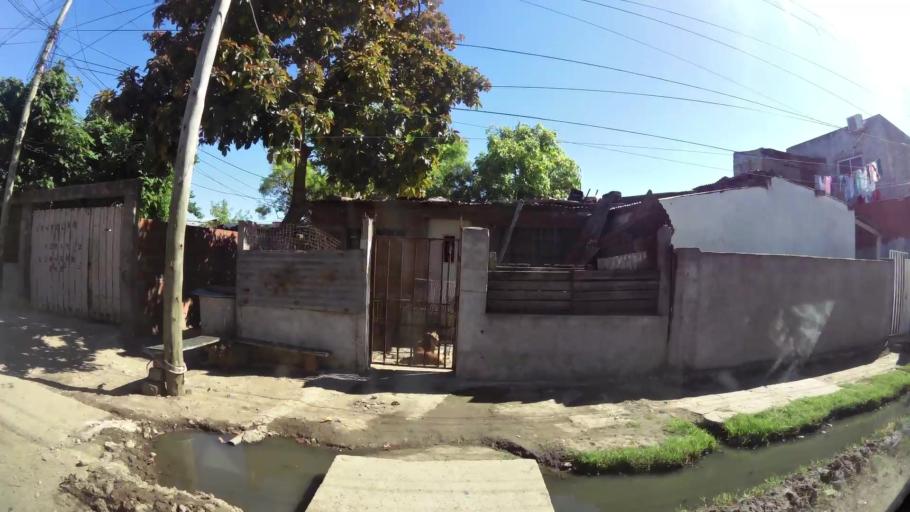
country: AR
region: Santa Fe
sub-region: Departamento de Rosario
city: Rosario
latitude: -32.9549
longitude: -60.6909
